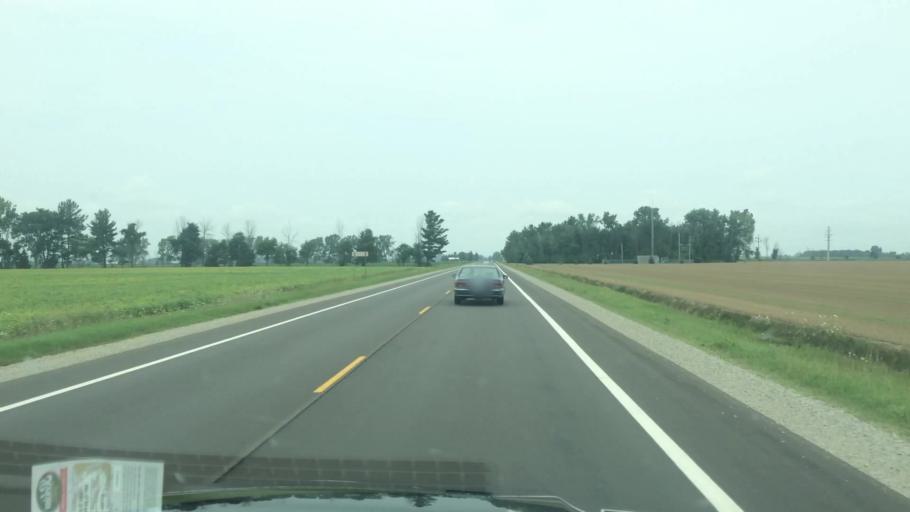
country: US
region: Michigan
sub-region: Huron County
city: Bad Axe
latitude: 43.9834
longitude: -83.0069
